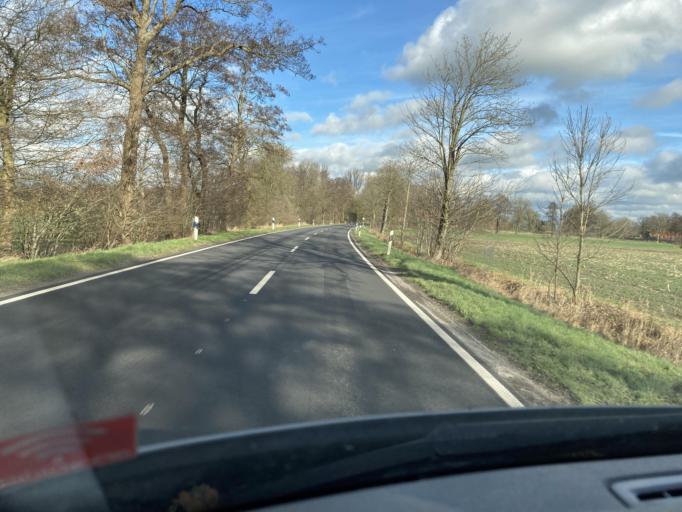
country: DE
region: Lower Saxony
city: Ostrhauderfehn
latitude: 53.1723
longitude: 7.5882
